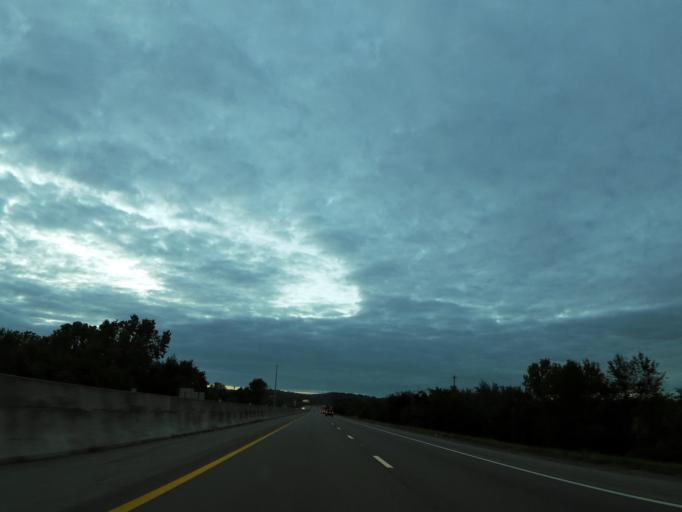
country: US
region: Tennessee
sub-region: Davidson County
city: Nashville
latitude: 36.1960
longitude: -86.8663
